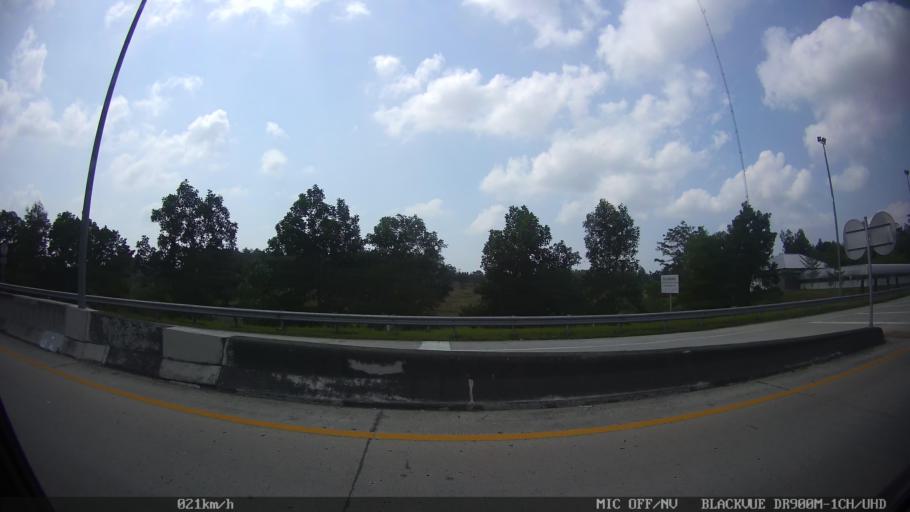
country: ID
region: Lampung
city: Natar
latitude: -5.2766
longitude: 105.2109
